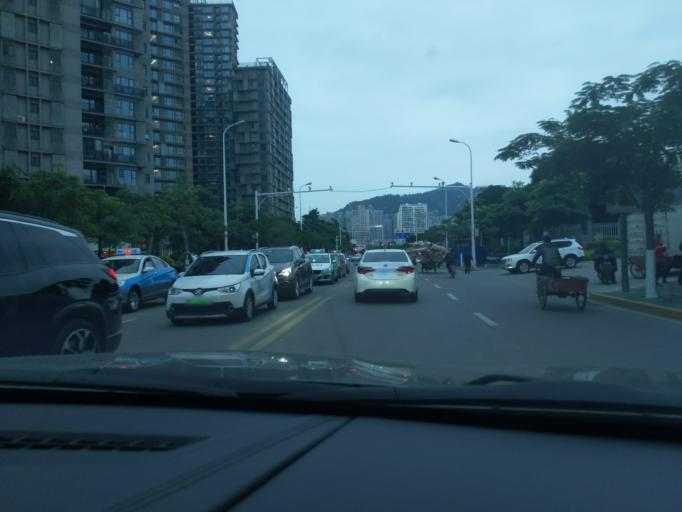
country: CN
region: Fujian
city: Xiamen
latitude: 24.4877
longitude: 118.1575
